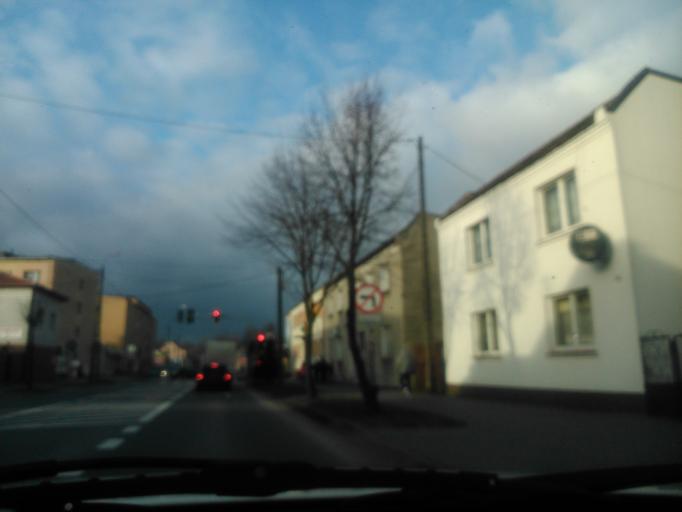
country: PL
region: Kujawsko-Pomorskie
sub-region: Powiat golubsko-dobrzynski
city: Golub-Dobrzyn
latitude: 53.1090
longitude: 19.0565
